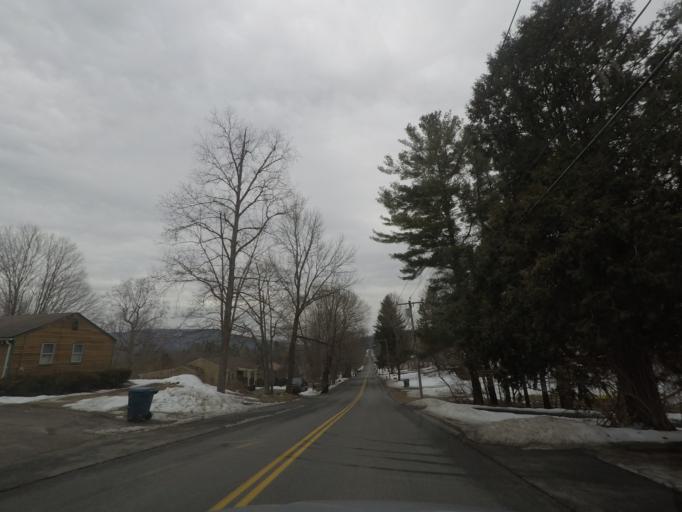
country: US
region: Massachusetts
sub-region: Berkshire County
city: Lee
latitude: 42.3067
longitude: -73.2560
